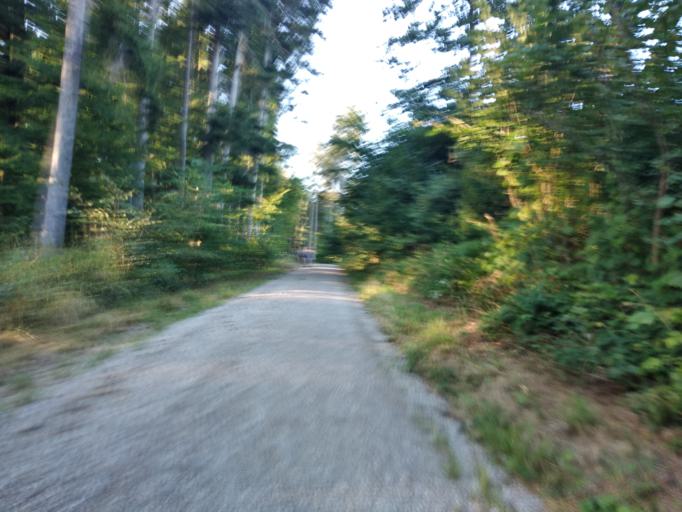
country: DE
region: Bavaria
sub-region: Swabia
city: Lautrach
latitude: 47.8891
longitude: 10.1042
